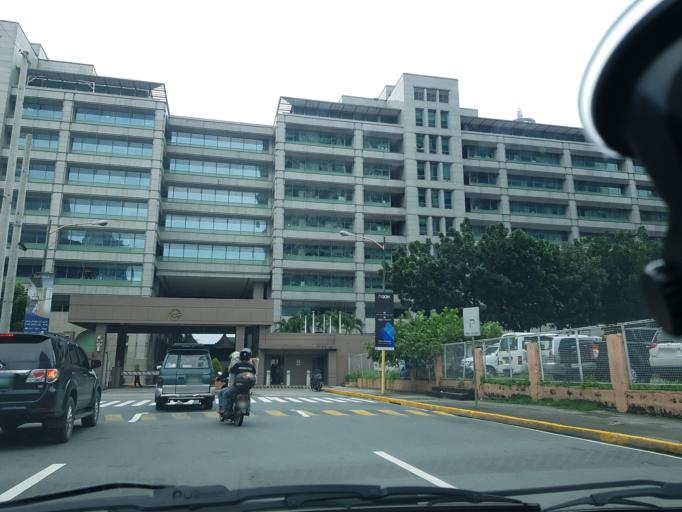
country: PH
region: Metro Manila
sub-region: Pasig
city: Pasig City
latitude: 14.5866
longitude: 121.0580
